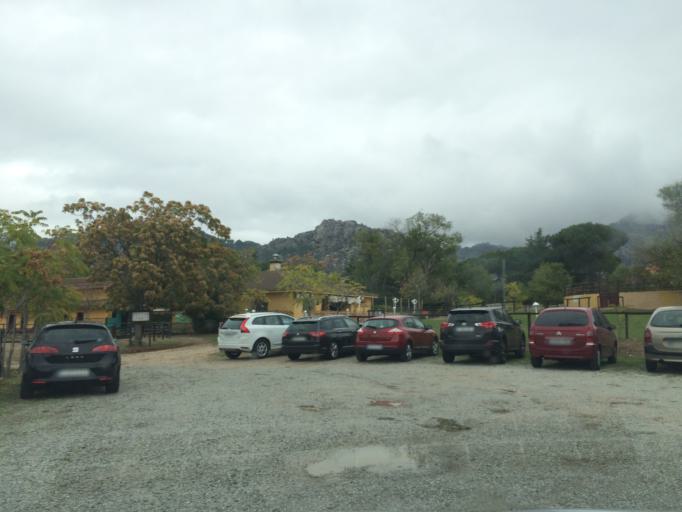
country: ES
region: Madrid
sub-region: Provincia de Madrid
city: Manzanares el Real
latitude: 40.7258
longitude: -3.8767
